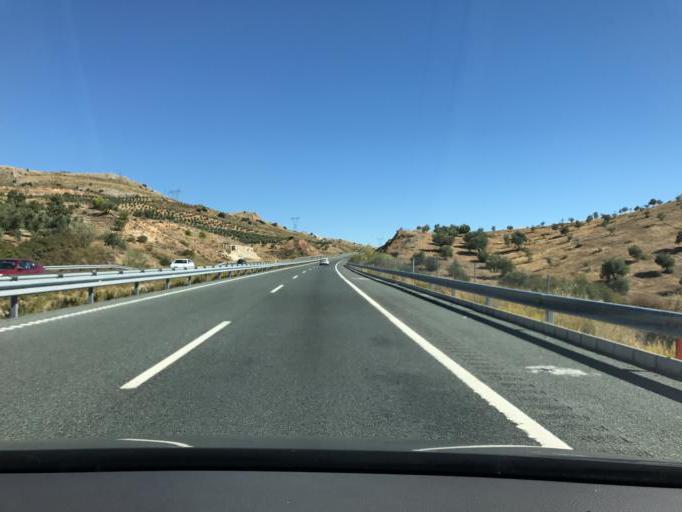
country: ES
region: Andalusia
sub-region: Provincia de Granada
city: Diezma
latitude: 37.3109
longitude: -3.3596
